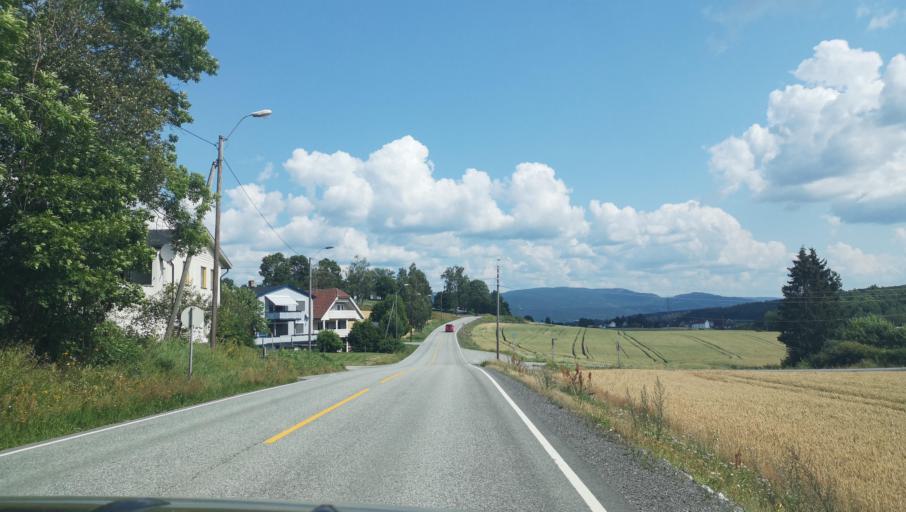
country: NO
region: Buskerud
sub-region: Ovre Eiker
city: Hokksund
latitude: 59.7376
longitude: 9.8564
